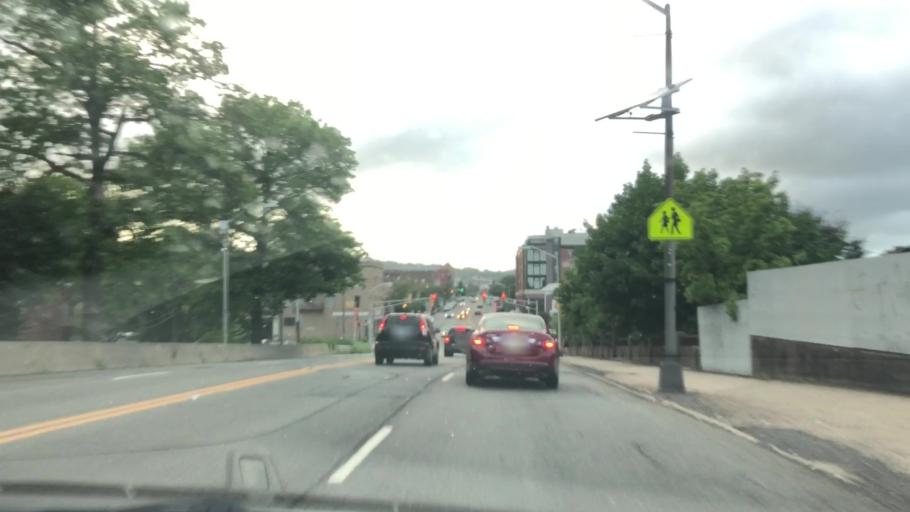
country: US
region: New Jersey
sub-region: Essex County
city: Glen Ridge
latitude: 40.8064
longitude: -74.2092
